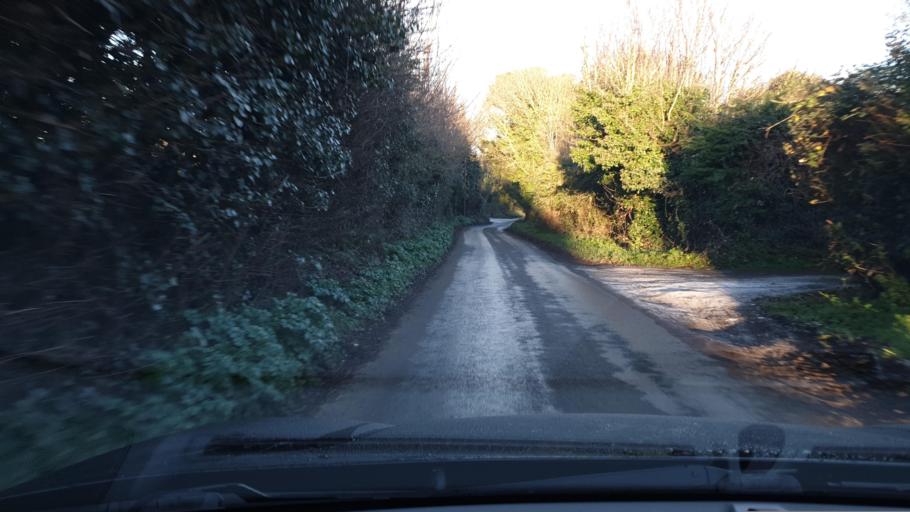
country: IE
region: Leinster
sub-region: Fingal County
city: Skerries
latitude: 53.5603
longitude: -6.1232
